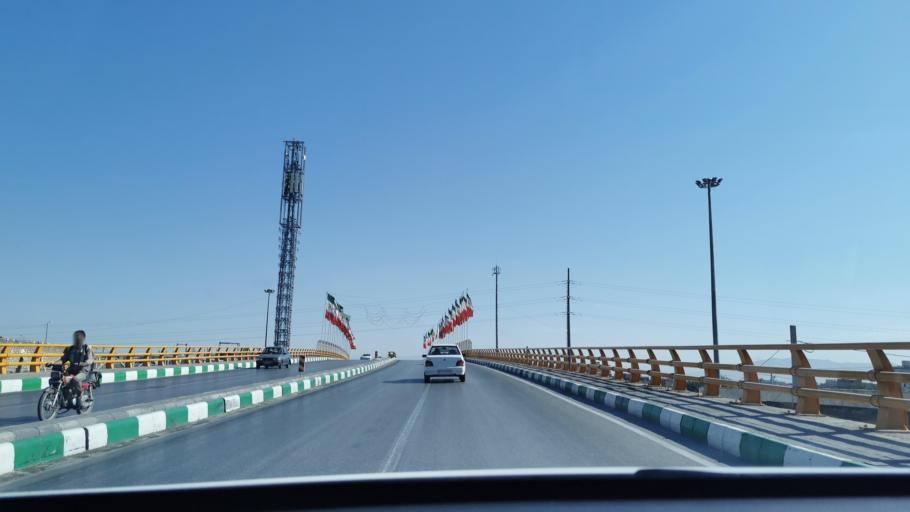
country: IR
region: Razavi Khorasan
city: Mashhad
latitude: 36.3179
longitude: 59.6395
